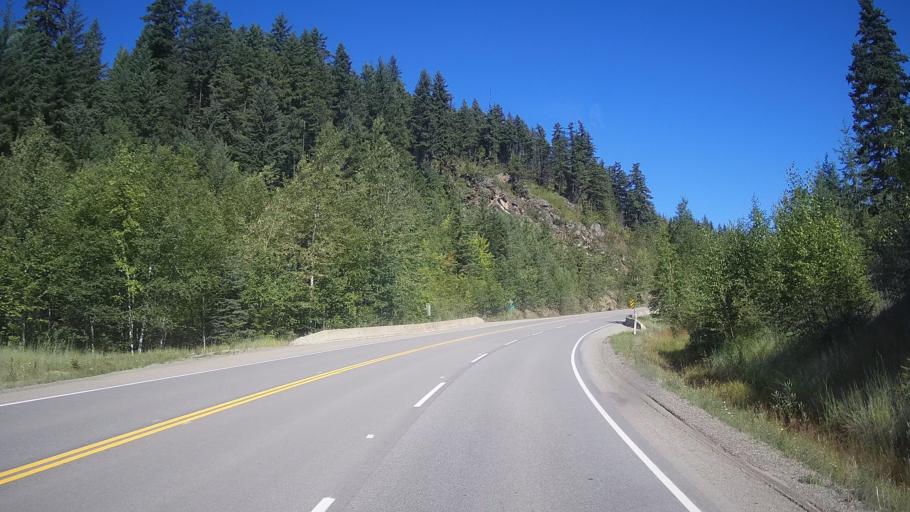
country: CA
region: British Columbia
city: Kamloops
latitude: 51.4626
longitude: -120.2473
